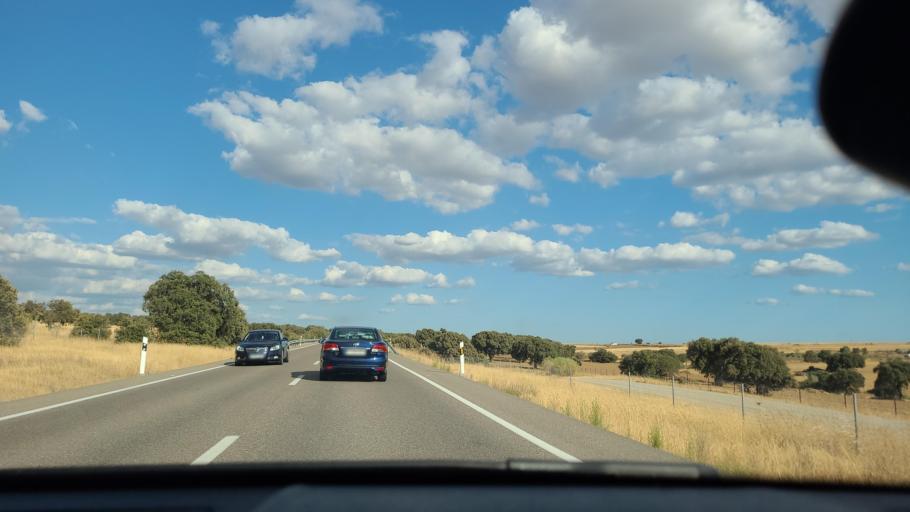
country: ES
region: Andalusia
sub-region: Province of Cordoba
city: Fuente Obejuna
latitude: 38.2642
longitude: -5.4942
